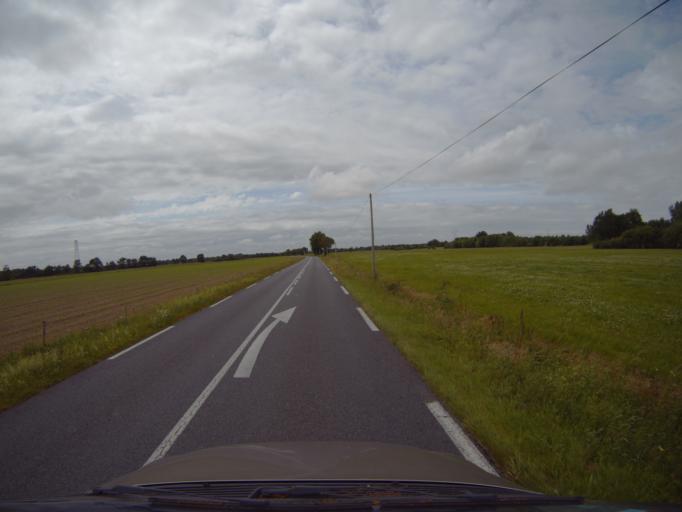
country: FR
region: Pays de la Loire
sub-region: Departement de la Loire-Atlantique
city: Montbert
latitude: 47.0597
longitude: -1.4463
